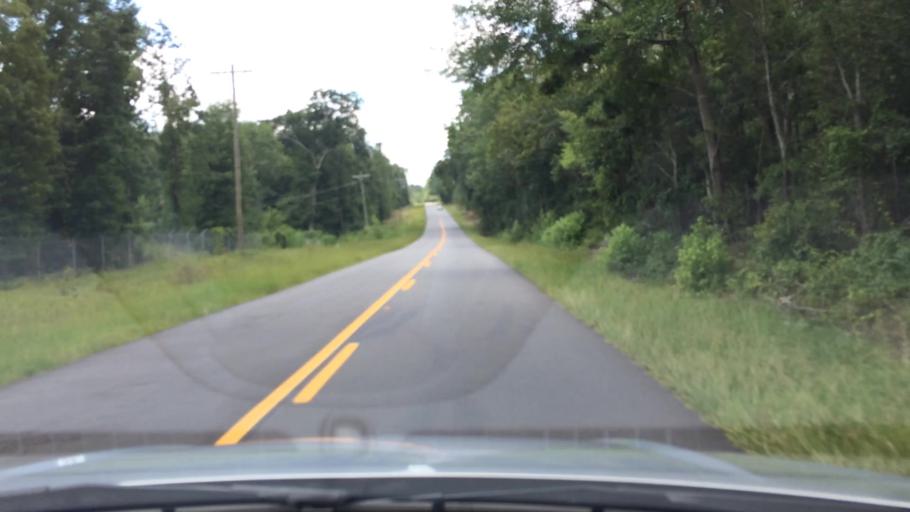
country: US
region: South Carolina
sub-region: Calhoun County
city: Oak Grove
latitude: 33.8075
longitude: -81.0090
